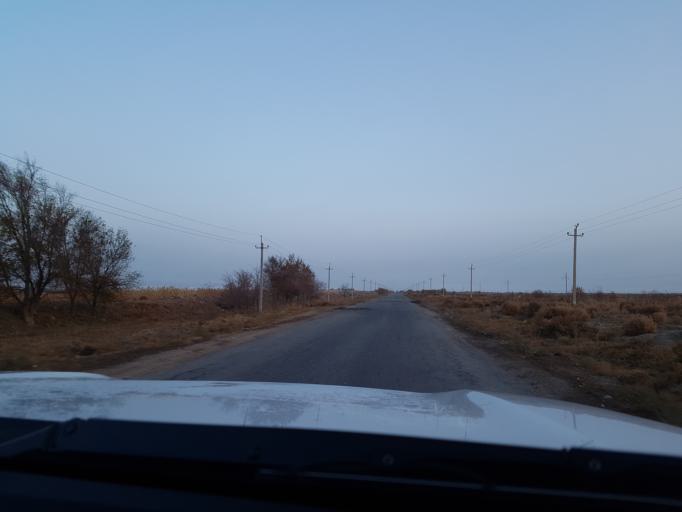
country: TM
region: Dasoguz
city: Koeneuergench
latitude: 41.7740
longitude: 58.6949
